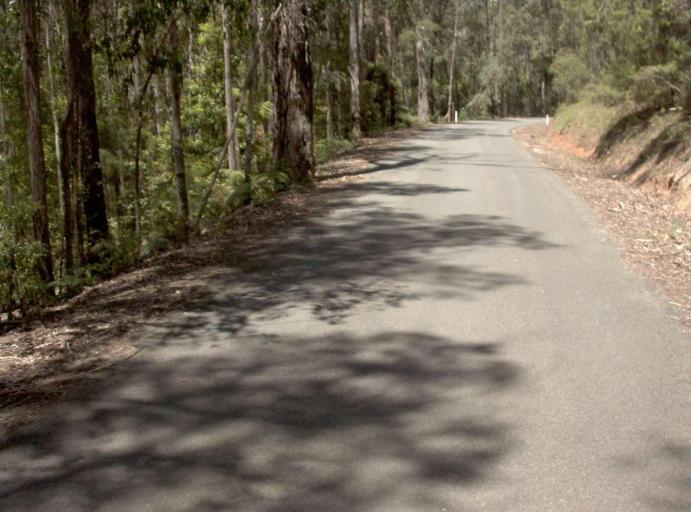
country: AU
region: New South Wales
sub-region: Bombala
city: Bombala
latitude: -37.5059
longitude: 148.9268
